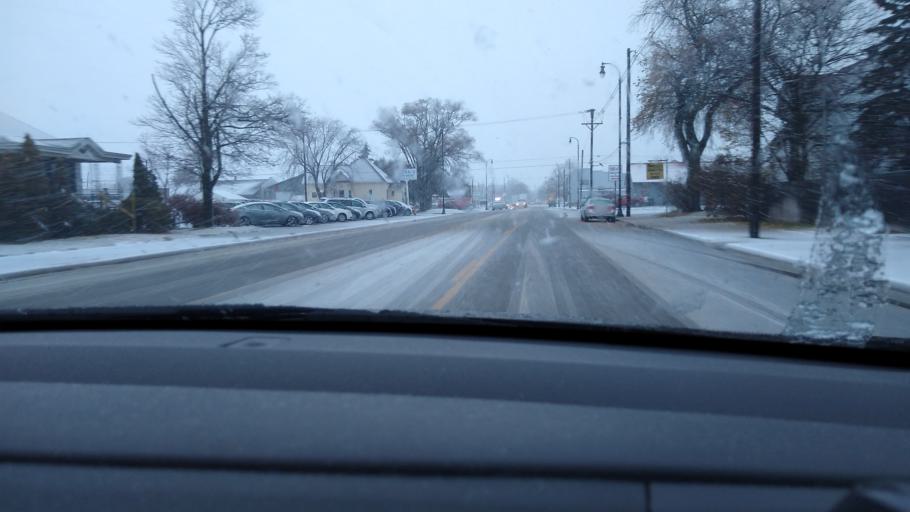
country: US
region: Michigan
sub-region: Delta County
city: Escanaba
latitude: 45.7528
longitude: -87.0718
